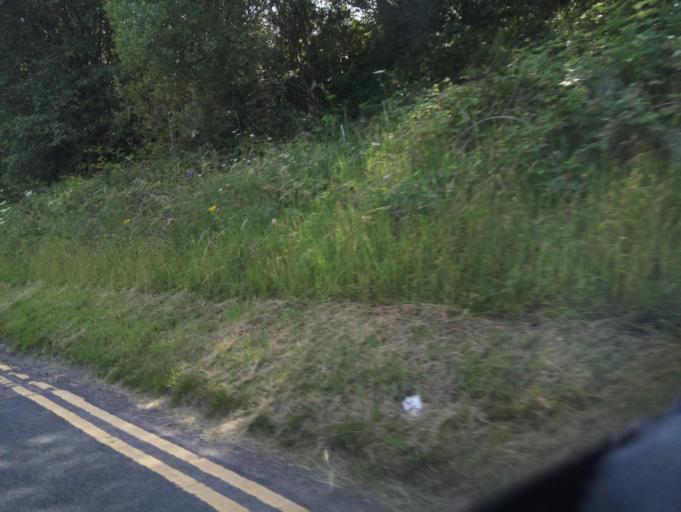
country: GB
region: Wales
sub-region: Caerphilly County Borough
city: New Tredegar
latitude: 51.7185
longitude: -3.2452
